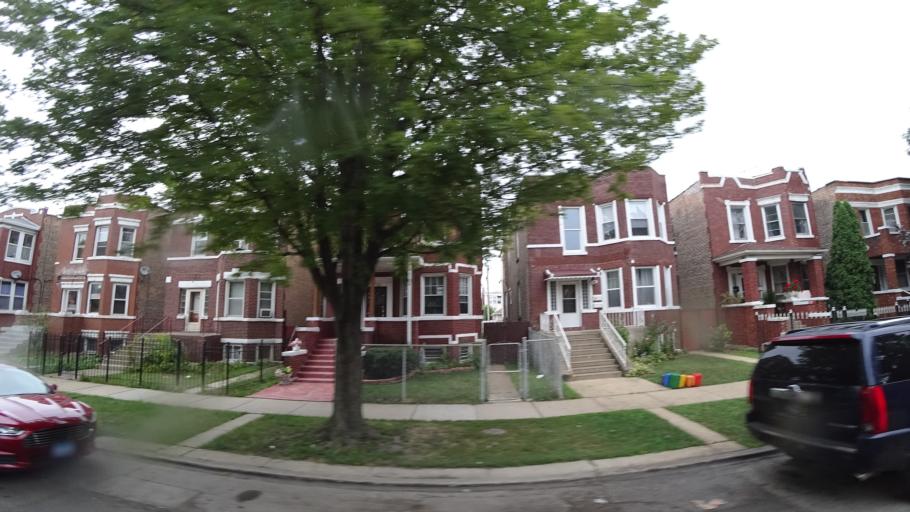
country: US
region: Illinois
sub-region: Cook County
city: Cicero
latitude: 41.8542
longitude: -87.7468
